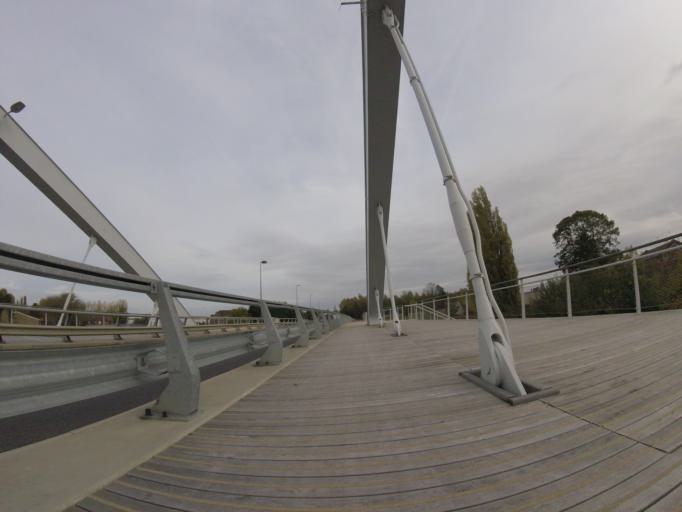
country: FR
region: Nord-Pas-de-Calais
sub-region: Departement du Nord
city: Erquinghem-Lys
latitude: 50.6906
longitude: 2.8605
